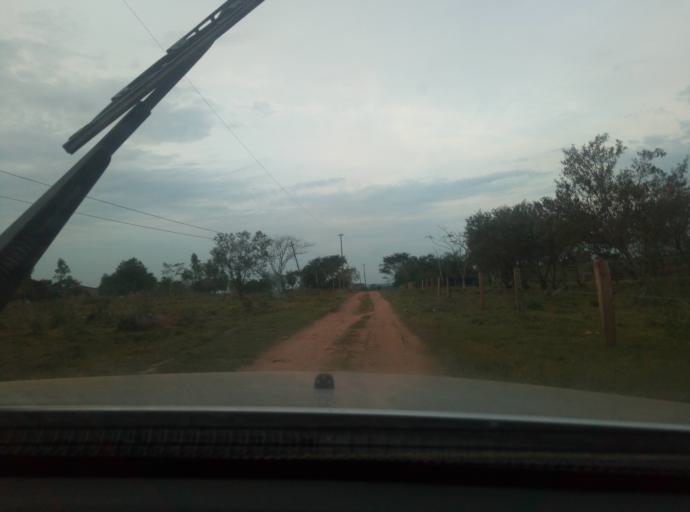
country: PY
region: Caaguazu
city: Carayao
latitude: -25.1485
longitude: -56.3845
